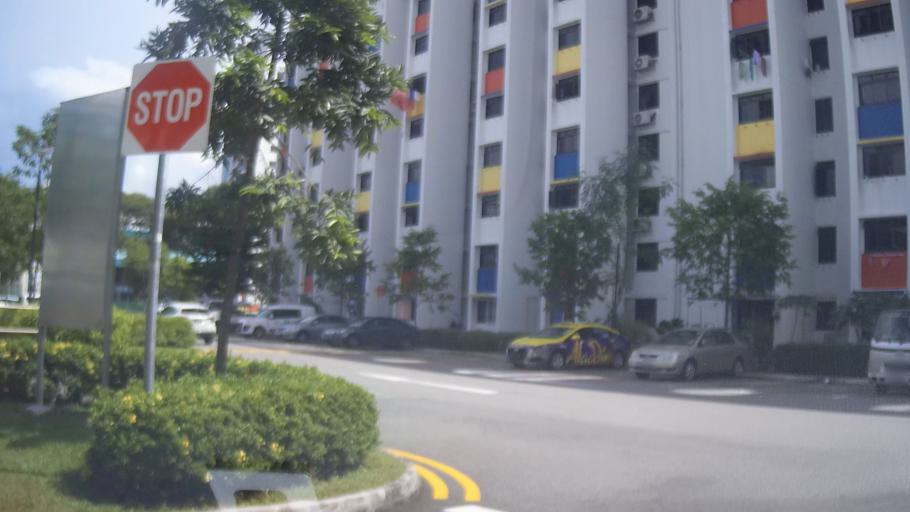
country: SG
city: Singapore
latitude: 1.3293
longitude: 103.8879
